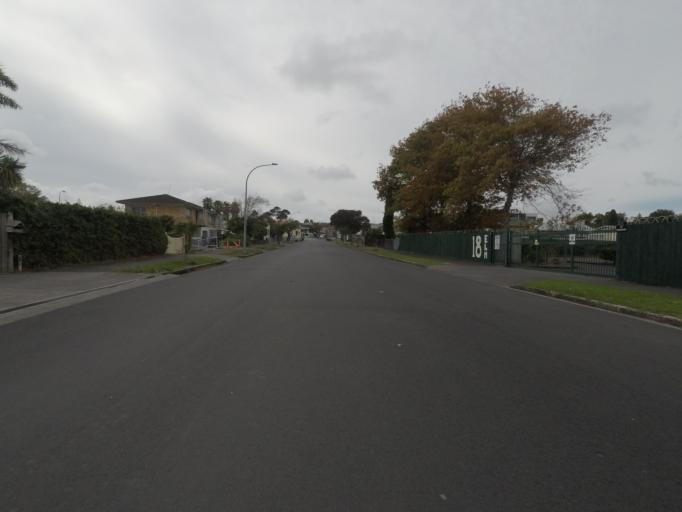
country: NZ
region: Auckland
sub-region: Auckland
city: Rosebank
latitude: -36.8952
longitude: 174.6942
